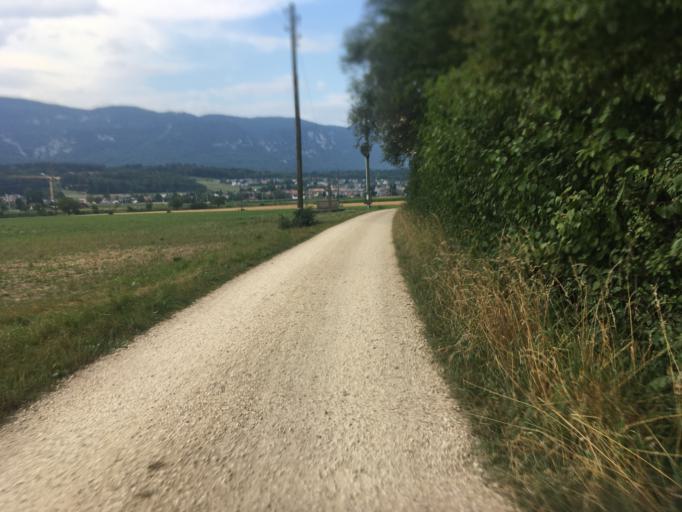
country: CH
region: Solothurn
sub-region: Bezirk Lebern
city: Selzach
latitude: 47.2033
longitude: 7.4842
